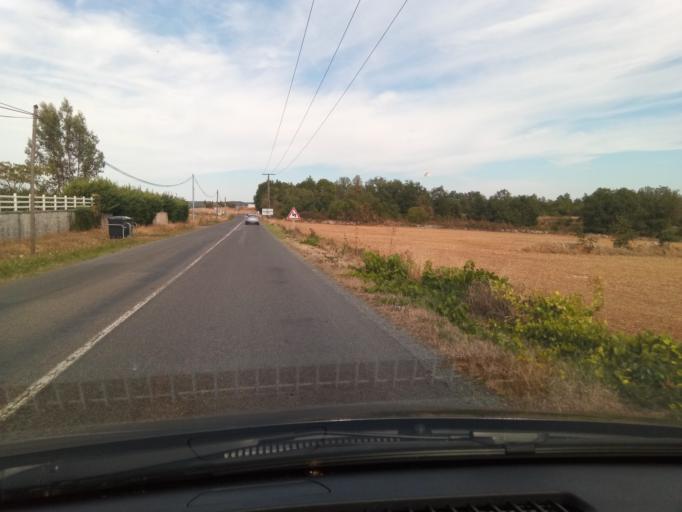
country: FR
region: Poitou-Charentes
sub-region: Departement de la Vienne
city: Chauvigny
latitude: 46.5592
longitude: 0.6167
